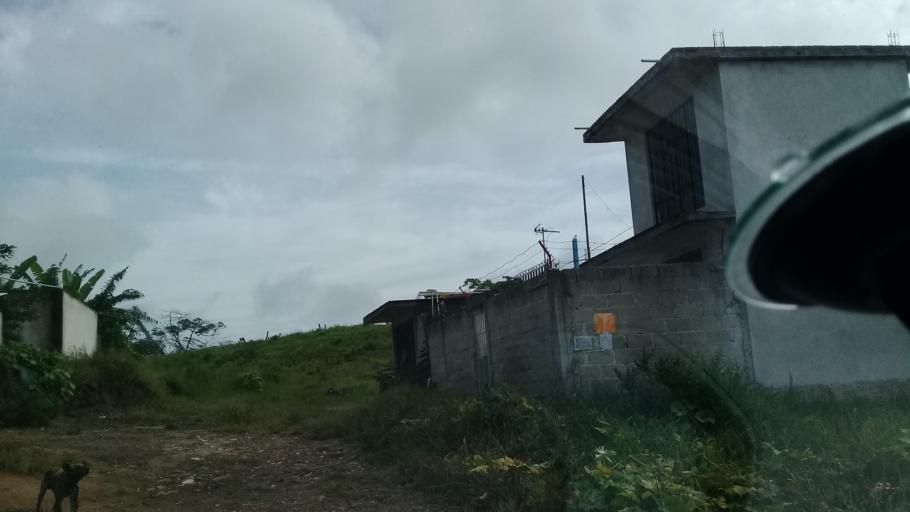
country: MX
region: Veracruz
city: El Castillo
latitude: 19.5534
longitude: -96.8785
